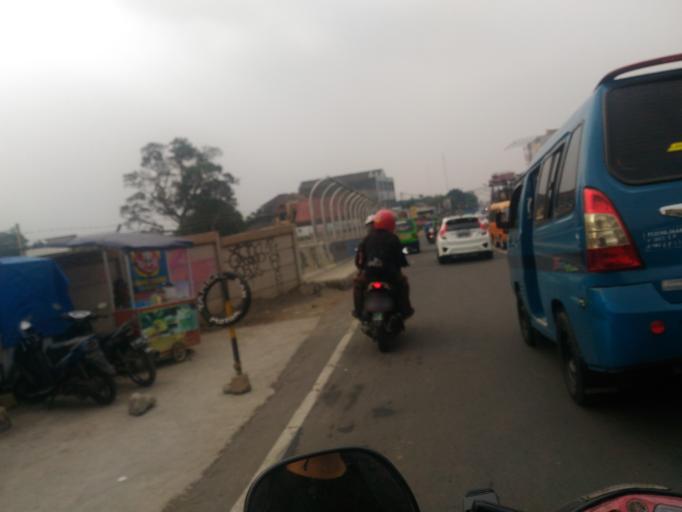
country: ID
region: West Java
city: Caringin
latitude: -6.6545
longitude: 106.8465
